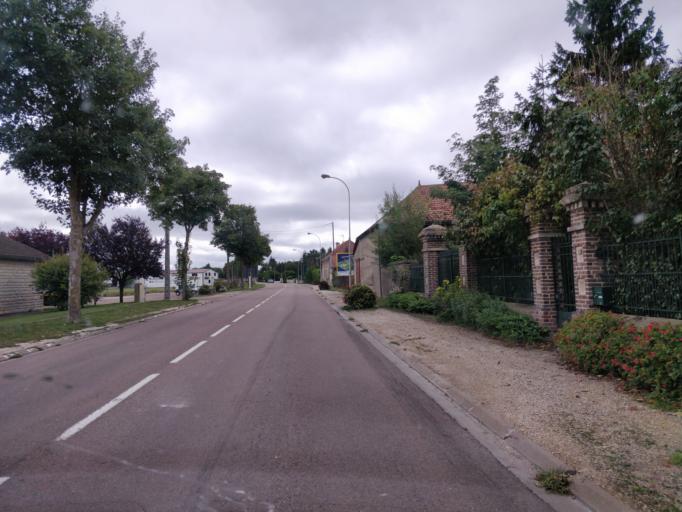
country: FR
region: Champagne-Ardenne
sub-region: Departement de l'Aube
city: Saint-Germain
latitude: 48.2565
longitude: 4.0296
